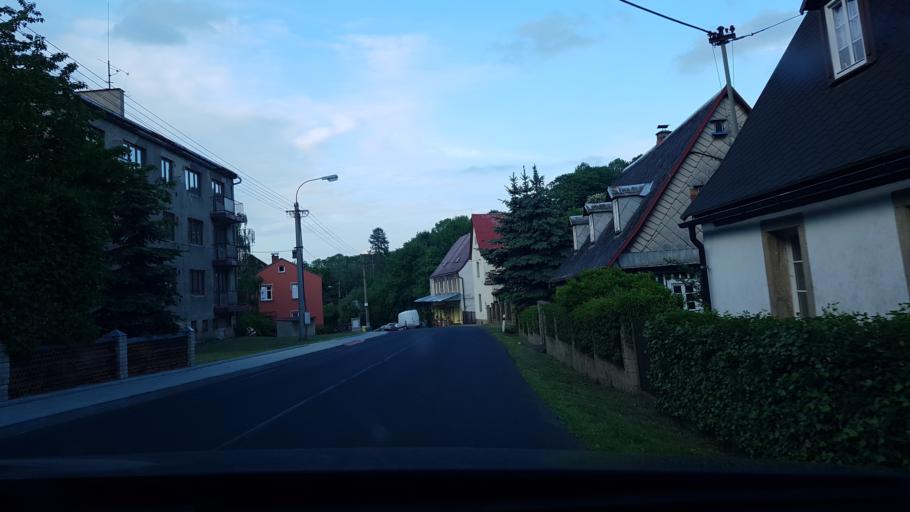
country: CZ
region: Ustecky
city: Libouchec
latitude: 50.8020
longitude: 13.9776
